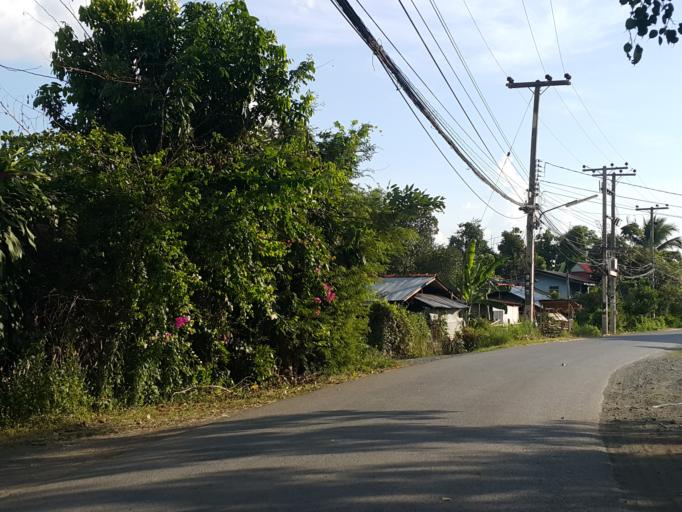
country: TH
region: Chiang Mai
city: San Kamphaeng
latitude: 18.8074
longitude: 99.1519
